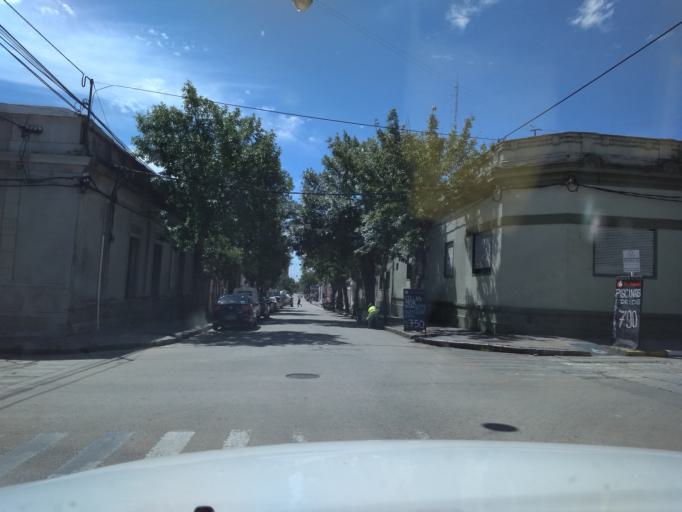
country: UY
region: Florida
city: Florida
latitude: -34.0965
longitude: -56.2161
